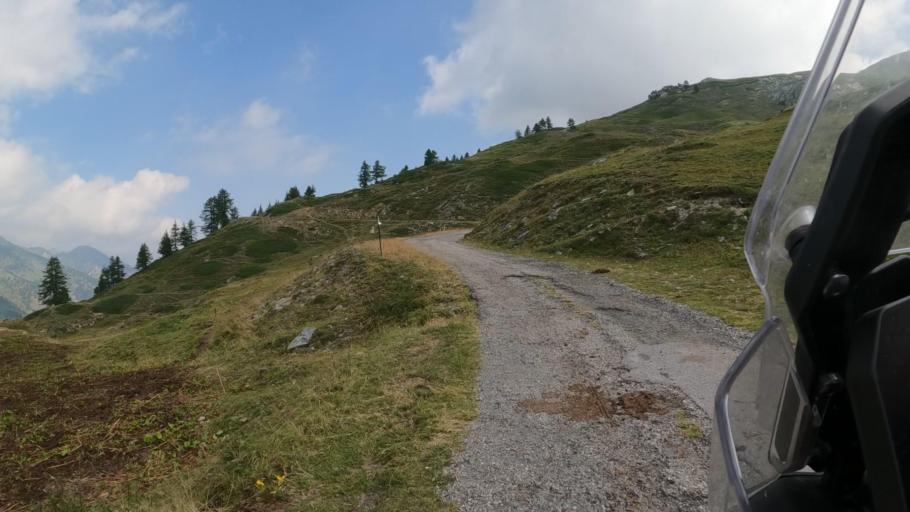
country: IT
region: Piedmont
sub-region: Provincia di Cuneo
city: Marmora
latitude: 44.4020
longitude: 7.1135
